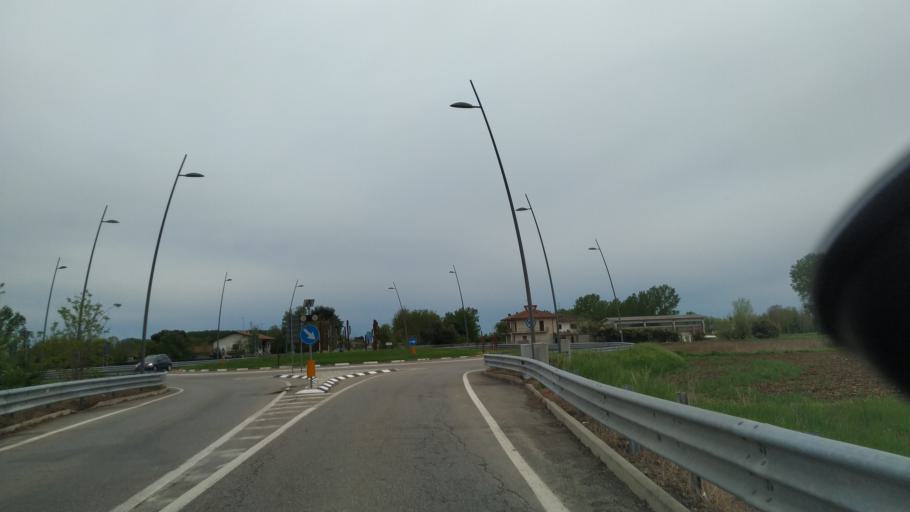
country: IT
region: Piedmont
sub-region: Provincia di Vercelli
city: Ghislarengo
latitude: 45.5229
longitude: 8.3861
